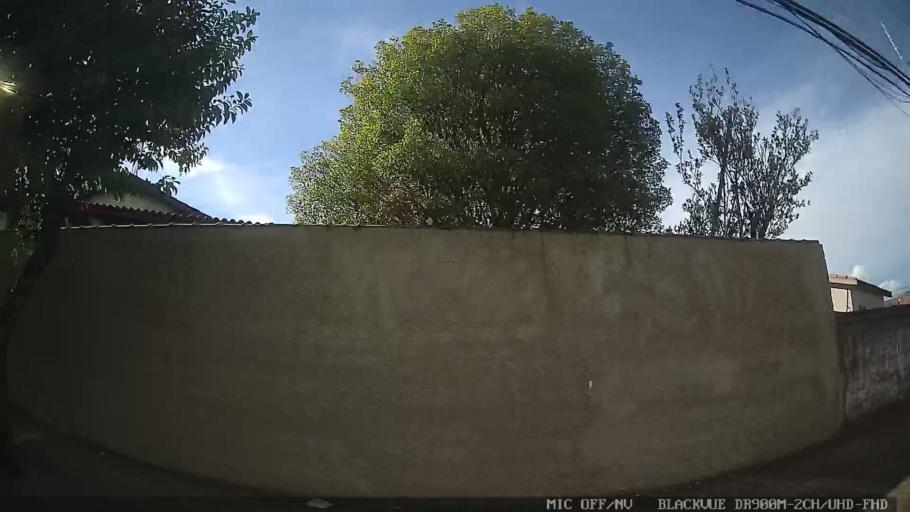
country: BR
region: Sao Paulo
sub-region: Tiete
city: Tiete
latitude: -23.0939
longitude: -47.7007
